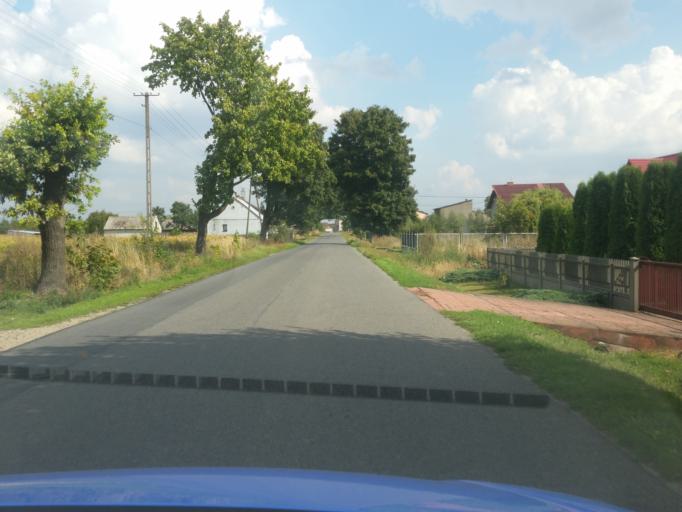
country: PL
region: Silesian Voivodeship
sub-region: Powiat czestochowski
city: Klomnice
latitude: 50.9647
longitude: 19.3329
